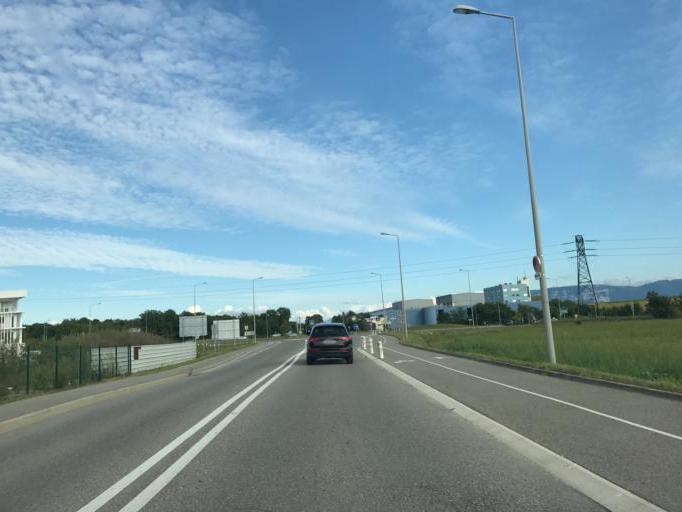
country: FR
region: Rhone-Alpes
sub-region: Departement de l'Ain
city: Saint-Genis-Pouilly
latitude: 46.2403
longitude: 6.0312
